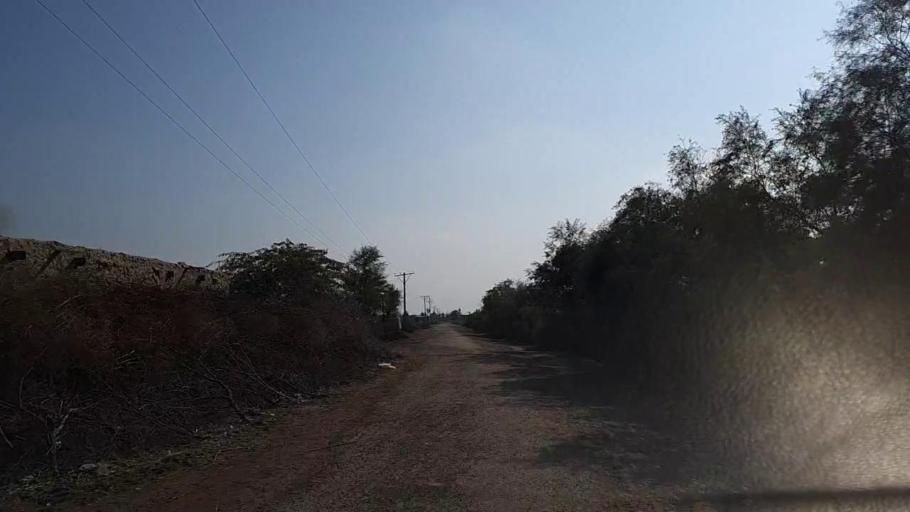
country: PK
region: Sindh
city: Jam Sahib
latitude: 26.2810
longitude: 68.6046
